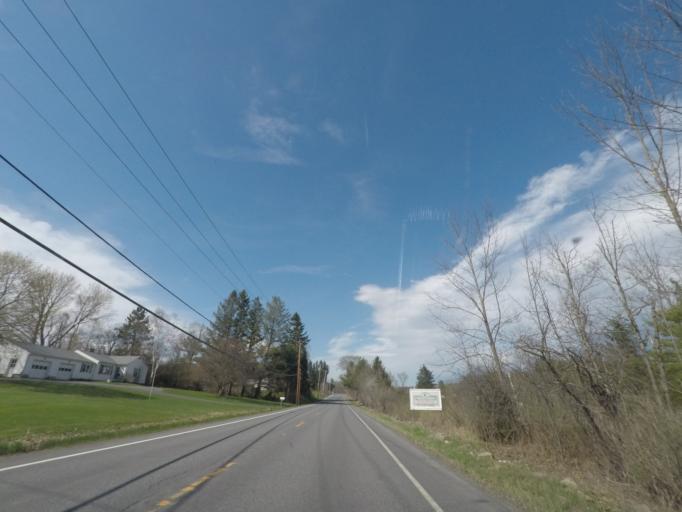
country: US
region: New York
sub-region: Greene County
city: Cairo
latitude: 42.4307
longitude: -74.0170
